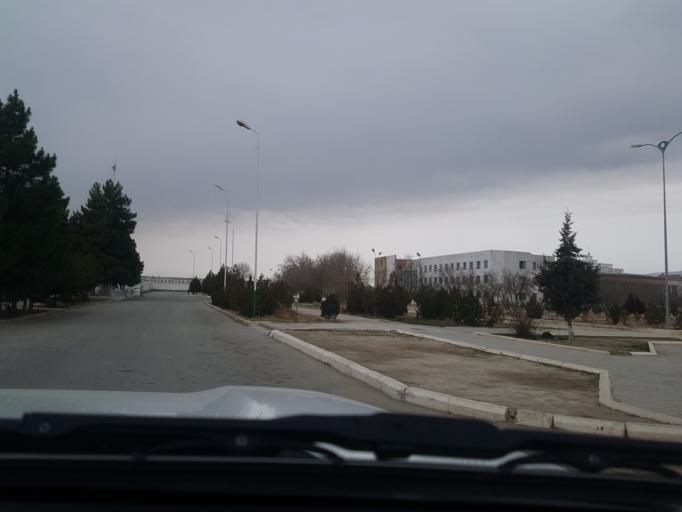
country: TM
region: Balkan
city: Balkanabat
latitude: 39.5141
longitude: 54.3559
